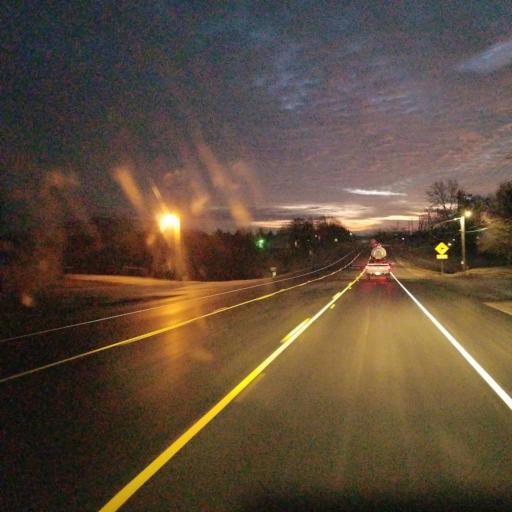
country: US
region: Illinois
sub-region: Peoria County
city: Hanna City
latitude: 40.6918
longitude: -89.7792
